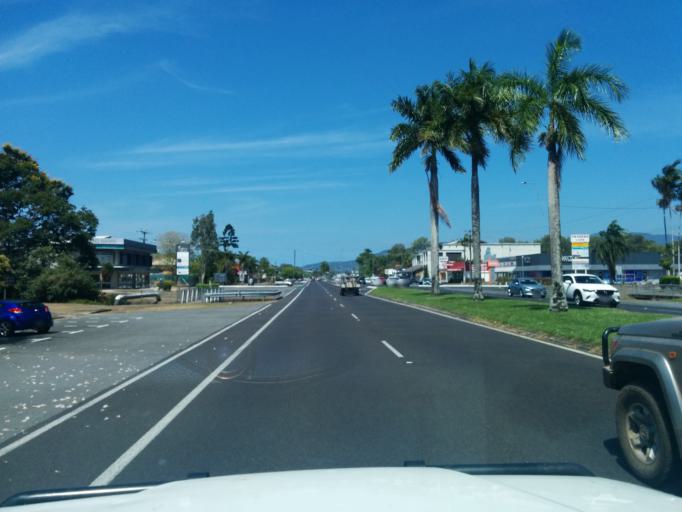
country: AU
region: Queensland
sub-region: Cairns
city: Cairns
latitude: -16.9165
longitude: 145.7440
